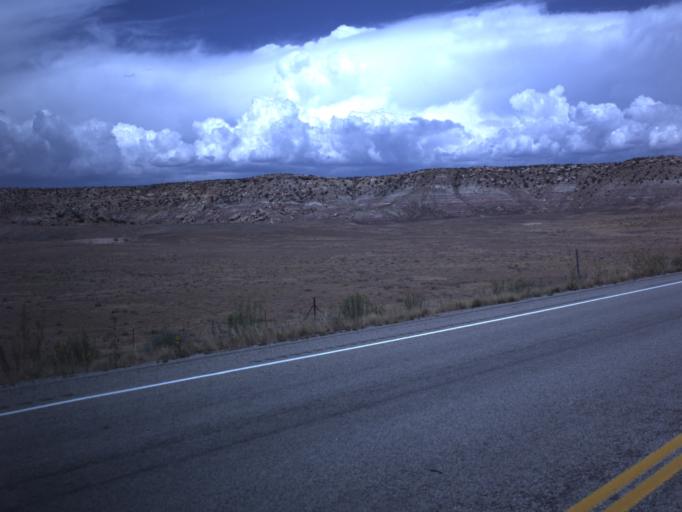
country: US
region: Utah
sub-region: San Juan County
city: Blanding
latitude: 37.4212
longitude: -109.4756
